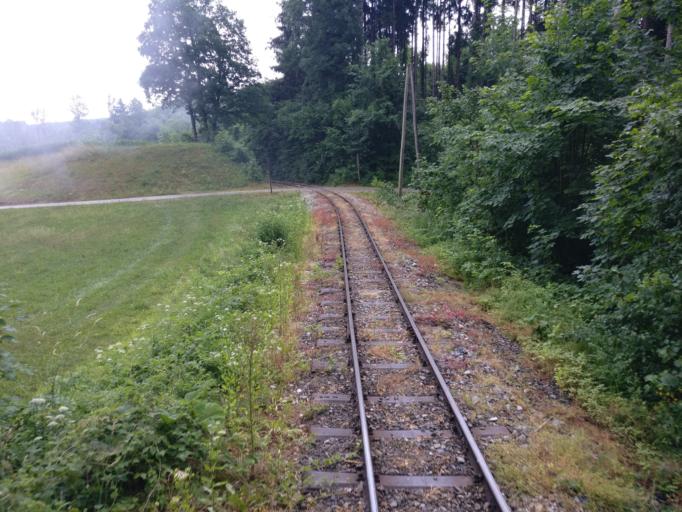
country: AT
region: Upper Austria
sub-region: Politischer Bezirk Steyr-Land
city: Waldneukirchen
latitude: 48.0029
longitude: 14.2954
